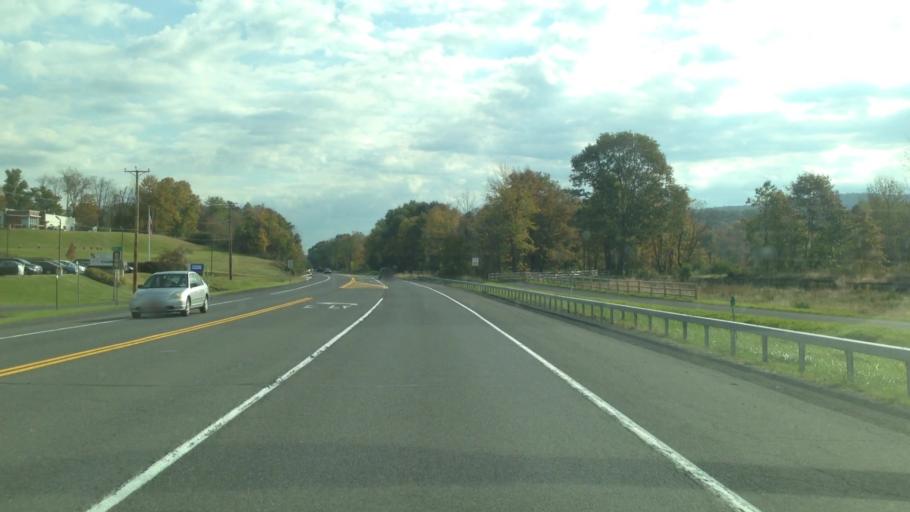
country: US
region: New York
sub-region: Ulster County
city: Clintondale
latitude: 41.7373
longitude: -74.0317
